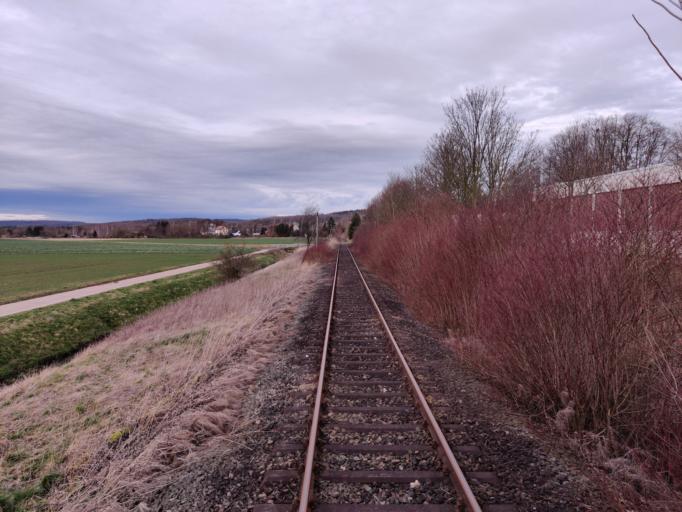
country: DE
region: Lower Saxony
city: Holle
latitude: 52.0922
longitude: 10.1513
